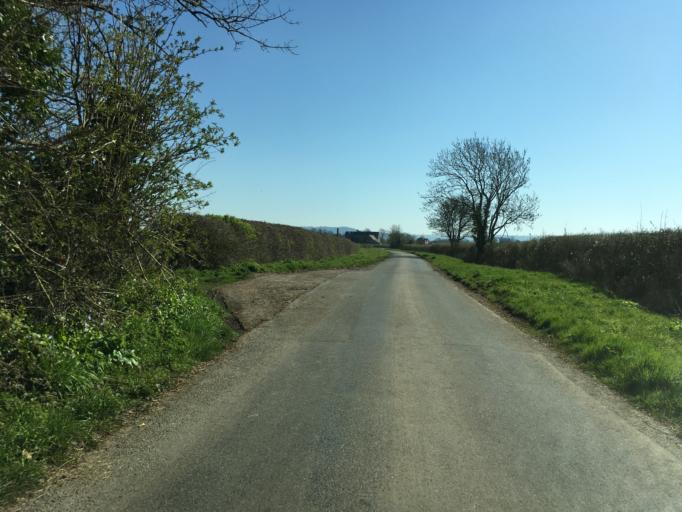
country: GB
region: England
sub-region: Gloucestershire
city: Berkeley
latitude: 51.6906
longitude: -2.4759
